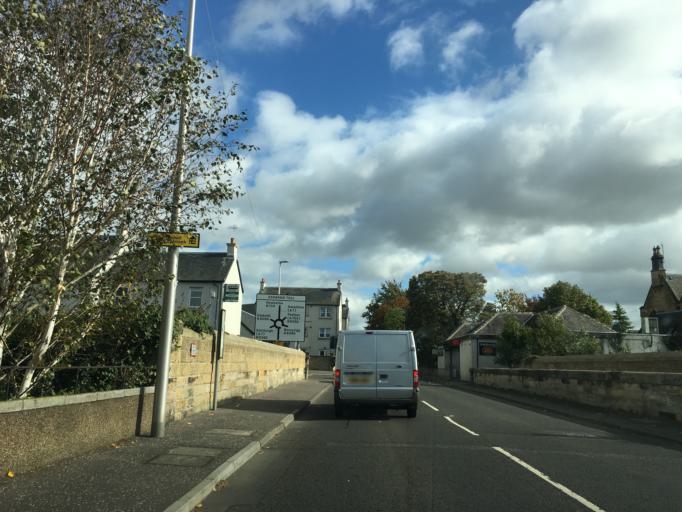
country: GB
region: Scotland
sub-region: Midlothian
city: Dalkeith
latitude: 55.8888
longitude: -3.0833
